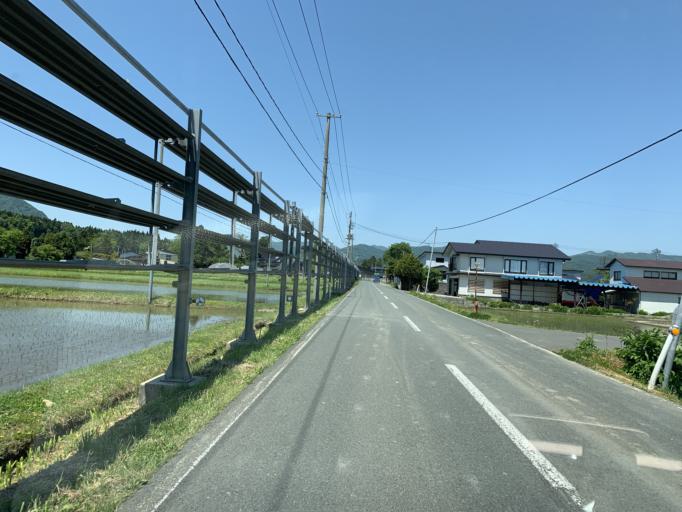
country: JP
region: Iwate
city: Kitakami
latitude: 39.2945
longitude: 140.9877
